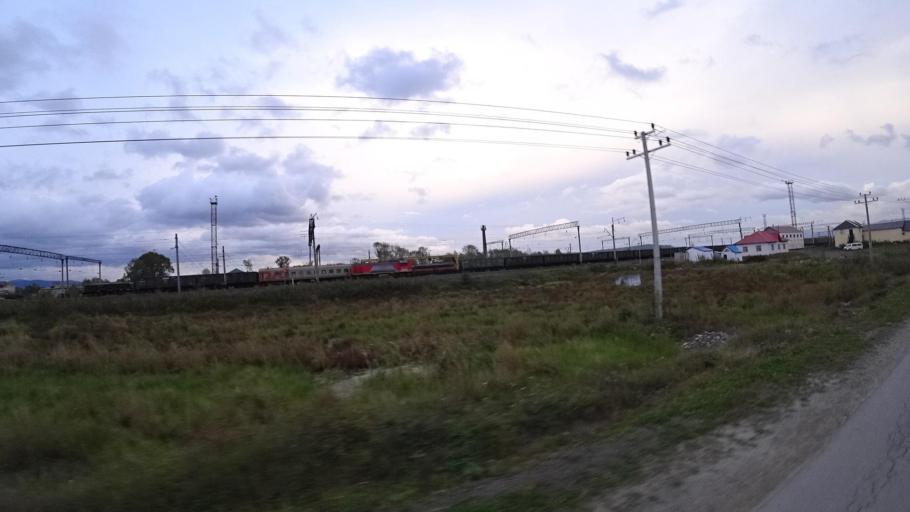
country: RU
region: Jewish Autonomous Oblast
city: Izvestkovyy
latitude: 48.9848
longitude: 131.5518
